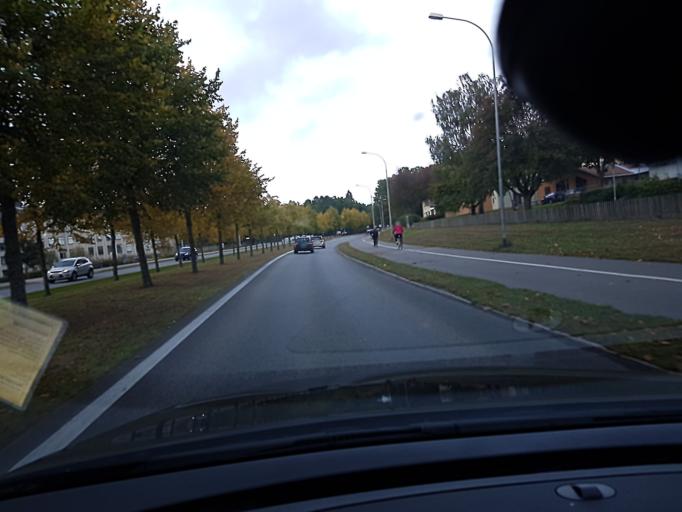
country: SE
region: Kronoberg
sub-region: Vaxjo Kommun
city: Vaexjoe
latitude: 56.8849
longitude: 14.8128
